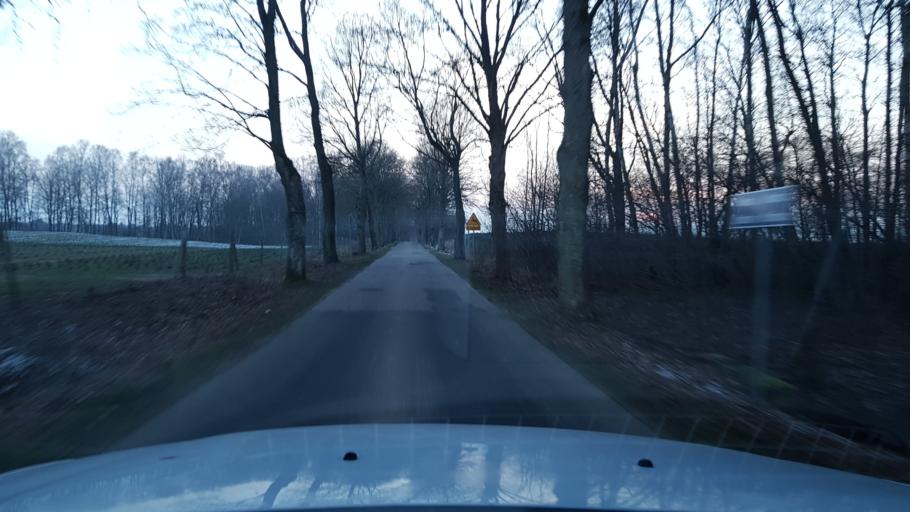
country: PL
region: West Pomeranian Voivodeship
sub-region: Powiat bialogardzki
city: Karlino
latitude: 54.0164
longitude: 15.8472
